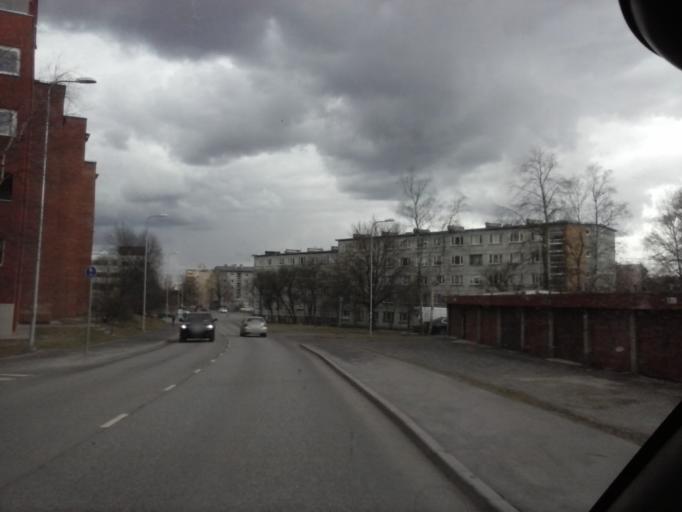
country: EE
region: Harju
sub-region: Tallinna linn
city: Tallinn
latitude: 59.4322
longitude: 24.7947
